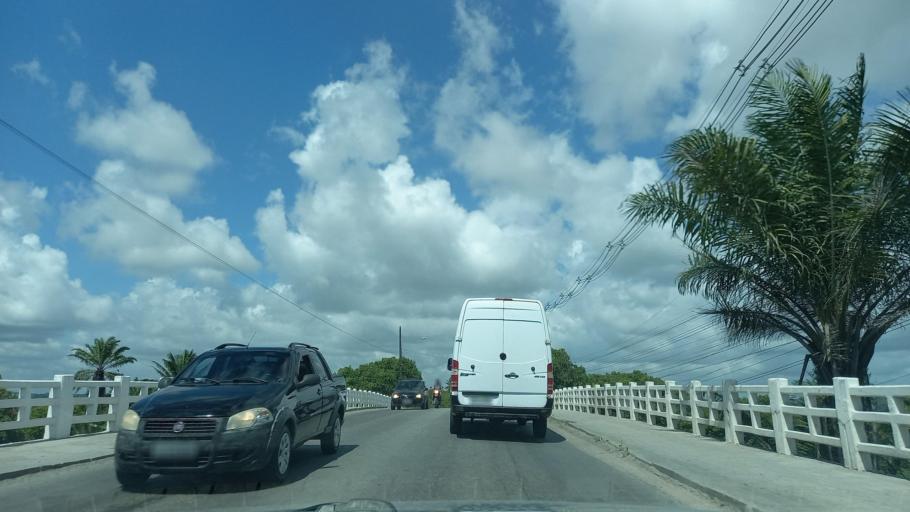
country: BR
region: Pernambuco
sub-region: Jaboatao Dos Guararapes
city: Jaboatao
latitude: -8.1551
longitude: -34.9502
